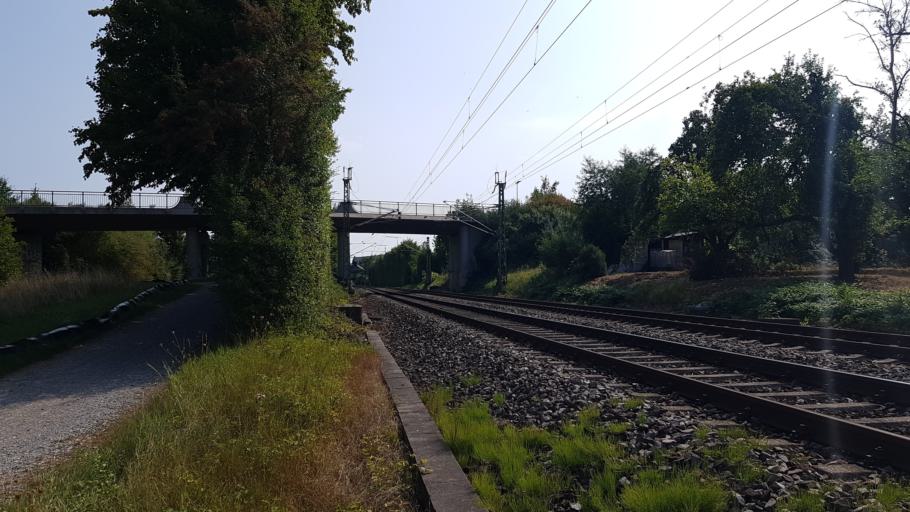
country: DE
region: Baden-Wuerttemberg
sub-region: Regierungsbezirk Stuttgart
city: Schorndorf
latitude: 48.8012
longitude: 9.5095
